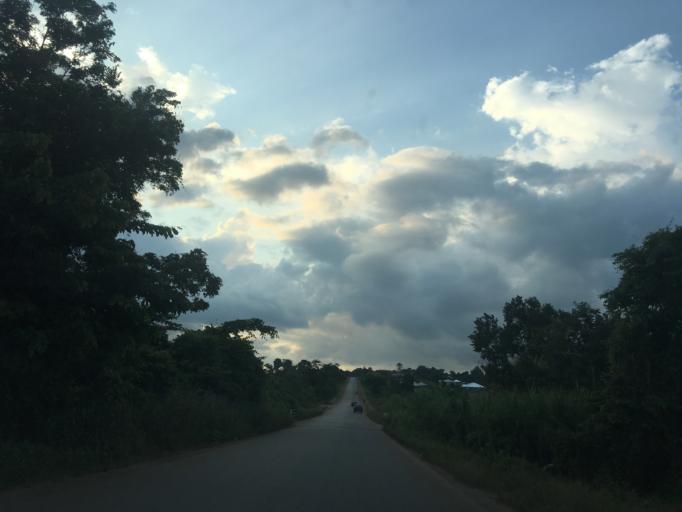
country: GH
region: Western
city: Bibiani
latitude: 6.7056
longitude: -2.4513
